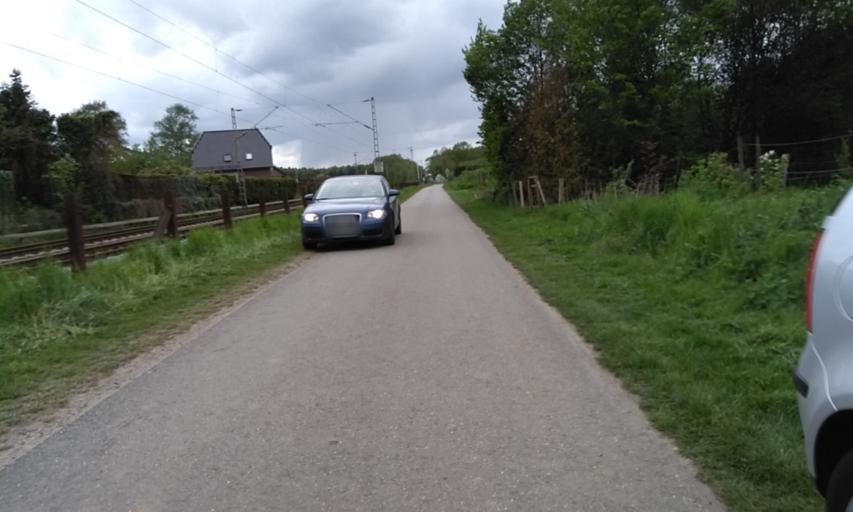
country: DE
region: Lower Saxony
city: Nottensdorf
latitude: 53.4875
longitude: 9.6243
